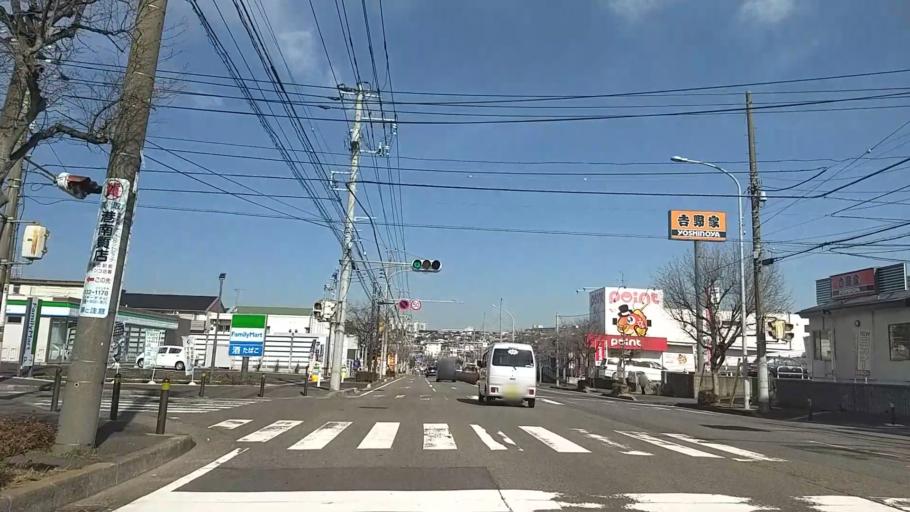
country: JP
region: Kanagawa
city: Kamakura
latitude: 35.3783
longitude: 139.5800
